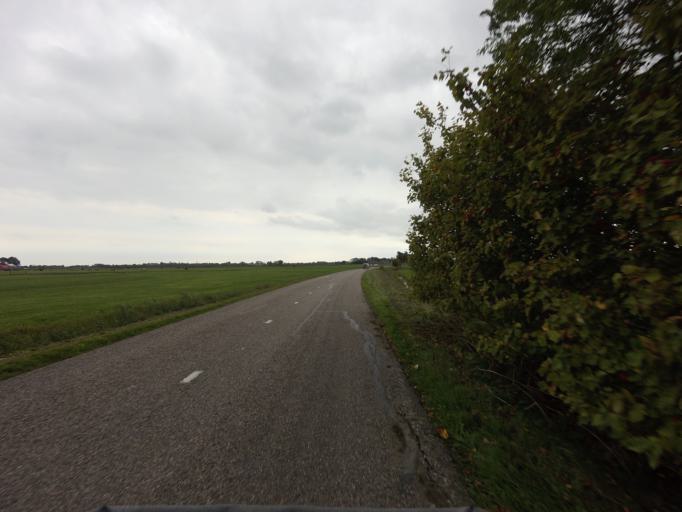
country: NL
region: Friesland
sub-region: Sudwest Fryslan
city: IJlst
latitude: 53.0233
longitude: 5.5974
